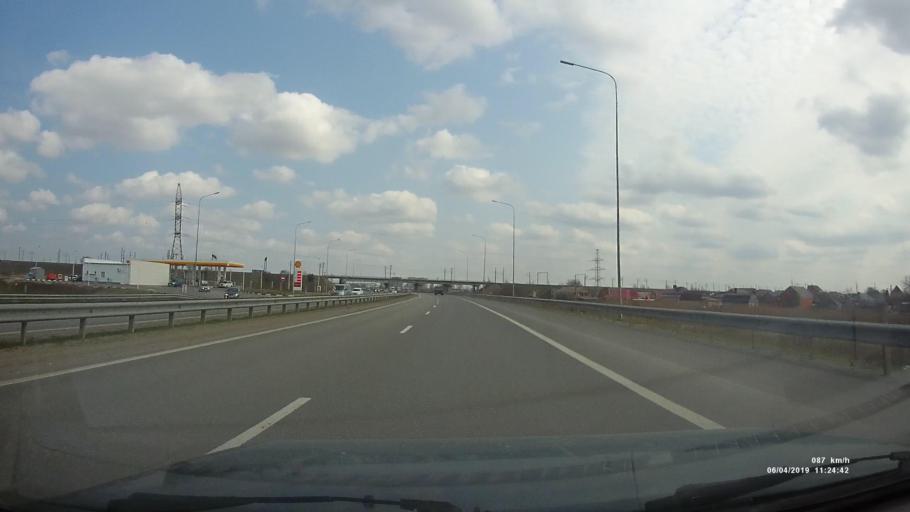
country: RU
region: Rostov
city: Bataysk
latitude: 47.1422
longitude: 39.6952
